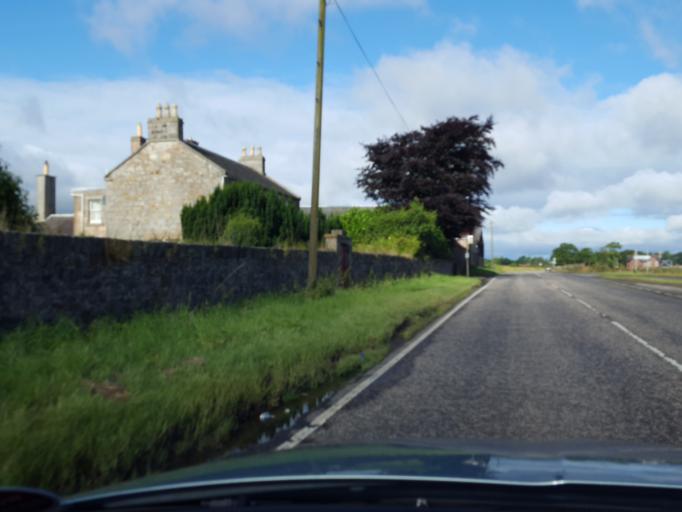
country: GB
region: Scotland
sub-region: West Lothian
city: Broxburn
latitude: 55.9658
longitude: -3.5231
